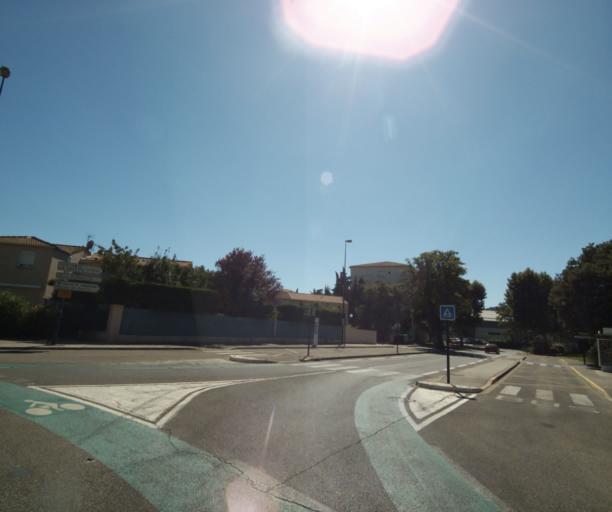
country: FR
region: Provence-Alpes-Cote d'Azur
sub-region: Departement du Var
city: La Garde
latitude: 43.1287
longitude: 6.0192
